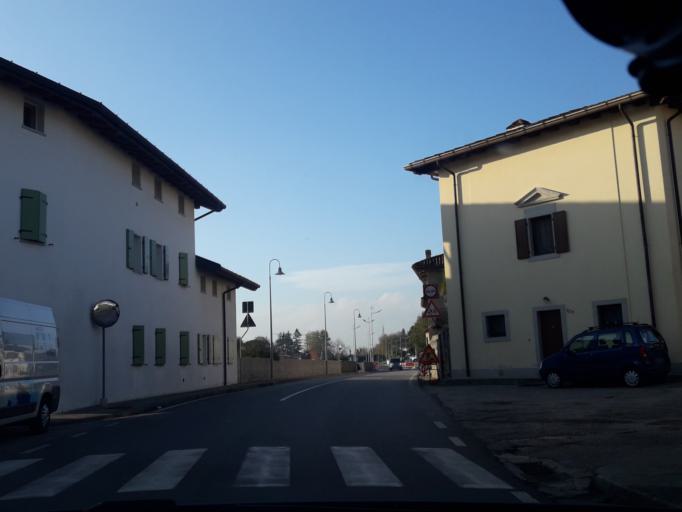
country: IT
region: Friuli Venezia Giulia
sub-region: Provincia di Udine
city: Pradamano
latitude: 46.0325
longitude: 13.3027
